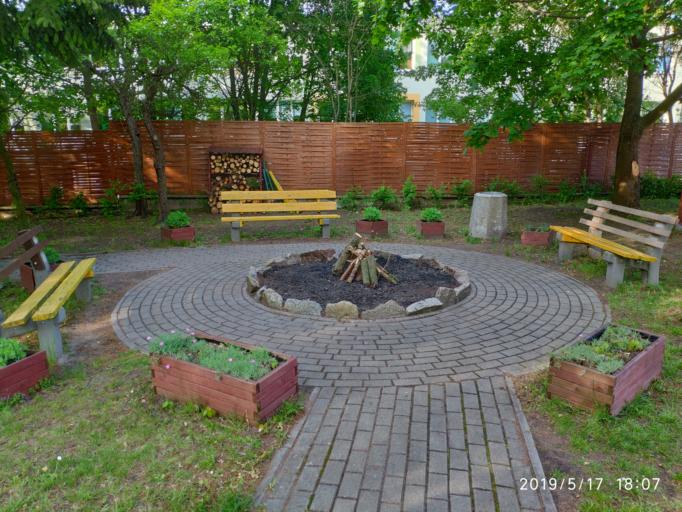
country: PL
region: Lubusz
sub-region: Zielona Gora
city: Zielona Gora
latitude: 51.9361
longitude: 15.5286
